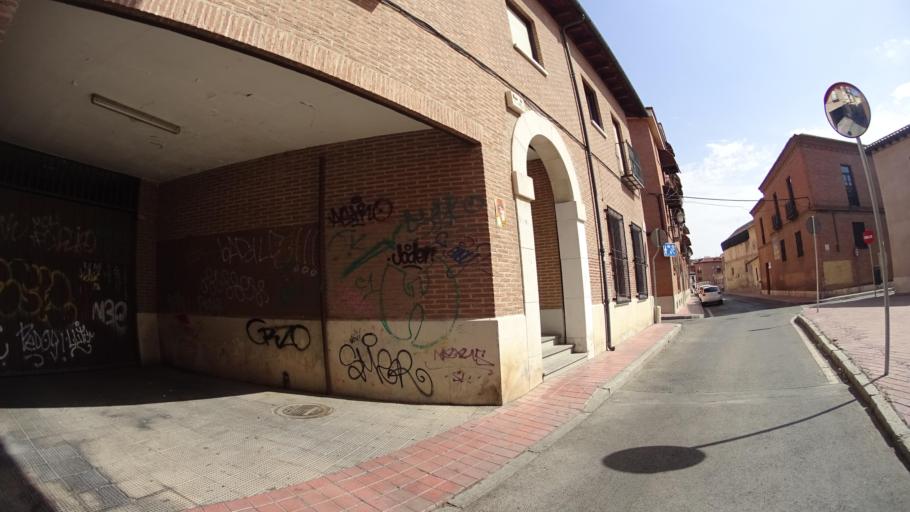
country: ES
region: Madrid
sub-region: Provincia de Madrid
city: Alcala de Henares
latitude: 40.4791
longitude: -3.3664
